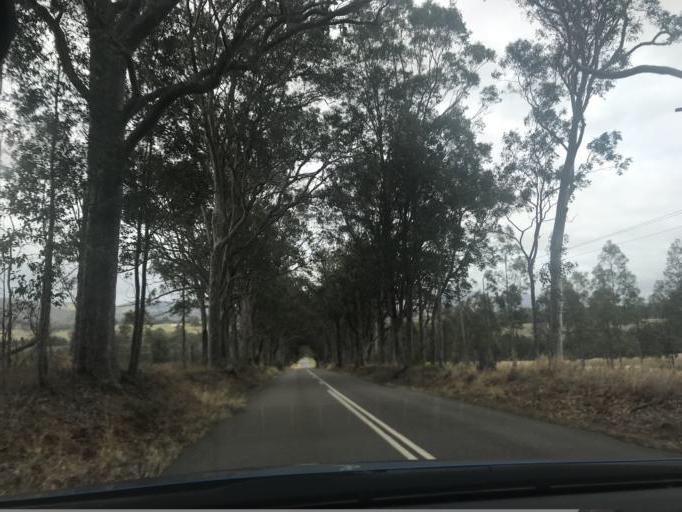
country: AU
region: New South Wales
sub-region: Cessnock
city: Cessnock
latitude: -32.8130
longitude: 151.3196
